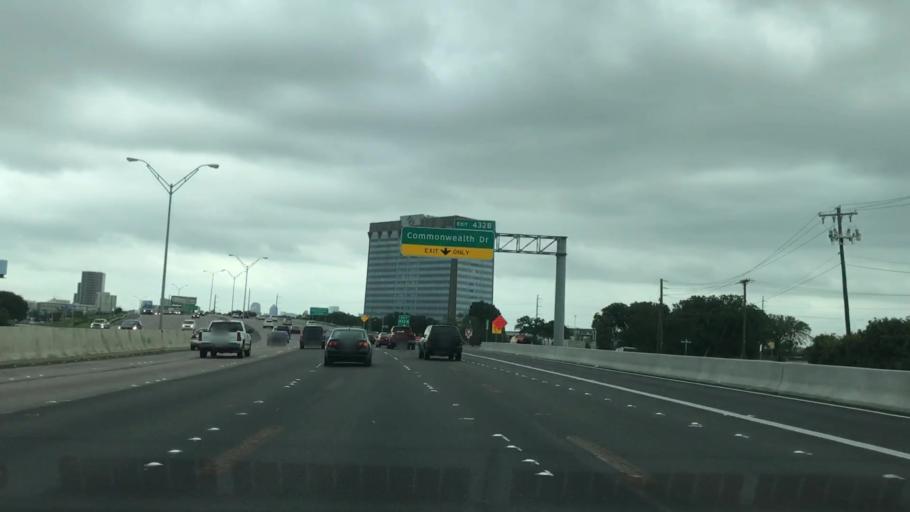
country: US
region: Texas
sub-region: Dallas County
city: Dallas
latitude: 32.8130
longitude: -96.8649
